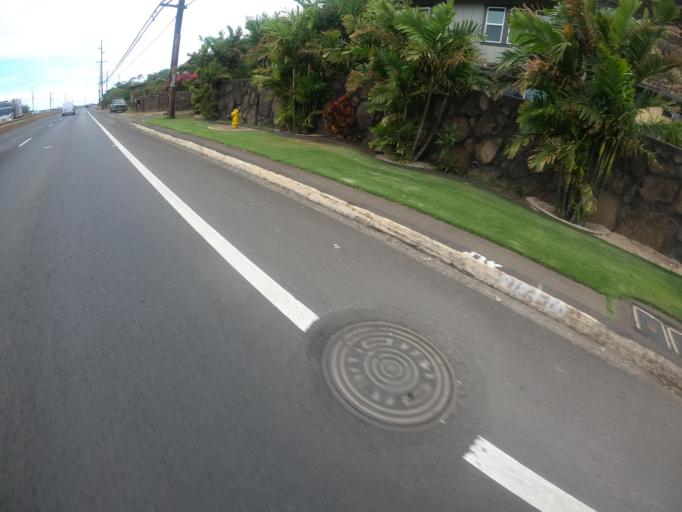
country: US
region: Hawaii
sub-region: Honolulu County
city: Nanakuli
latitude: 21.3983
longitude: -158.1694
